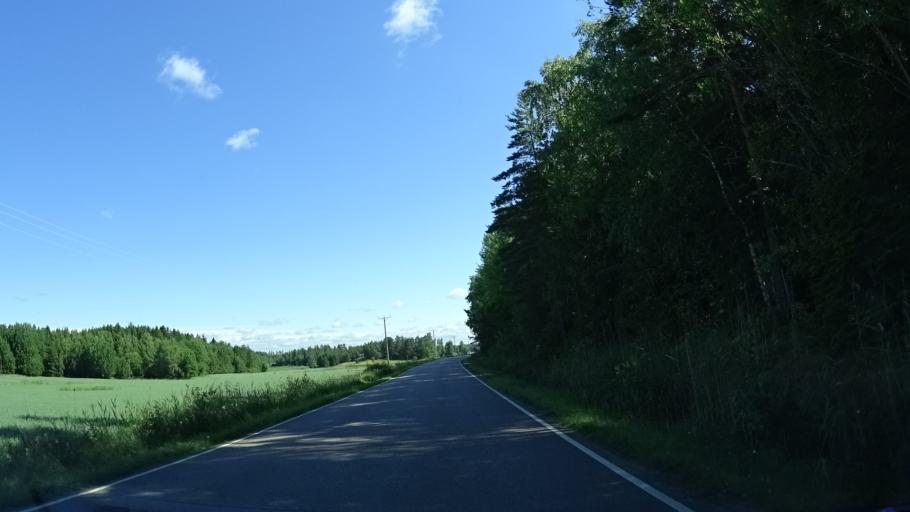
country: FI
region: Varsinais-Suomi
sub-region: Turku
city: Merimasku
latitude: 60.5238
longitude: 21.8285
